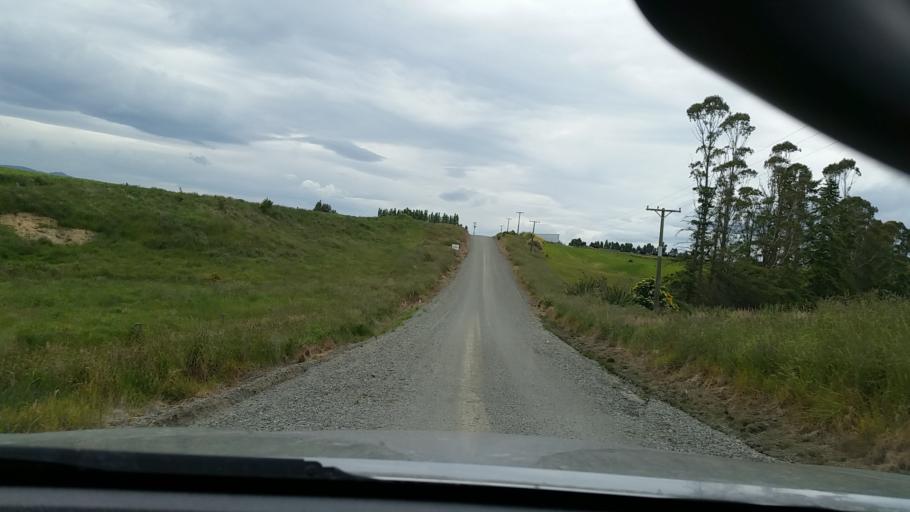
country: NZ
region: Southland
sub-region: Southland District
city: Winton
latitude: -45.9023
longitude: 168.1456
